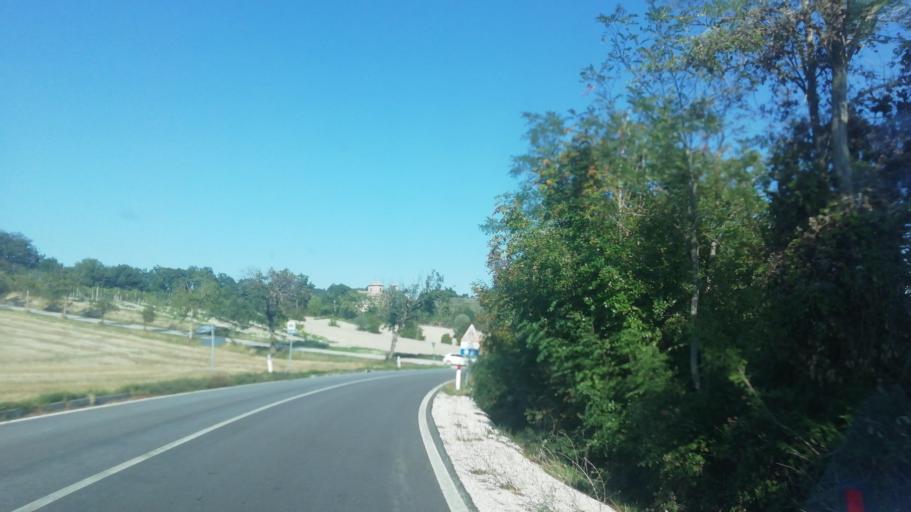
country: IT
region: The Marches
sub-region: Provincia di Pesaro e Urbino
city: Frontone
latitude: 43.5384
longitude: 12.7386
